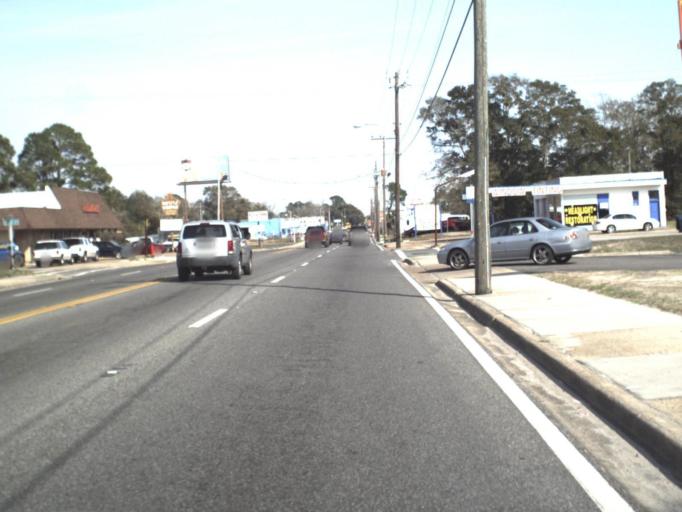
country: US
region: Florida
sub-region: Bay County
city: Cedar Grove
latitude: 30.1568
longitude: -85.6301
